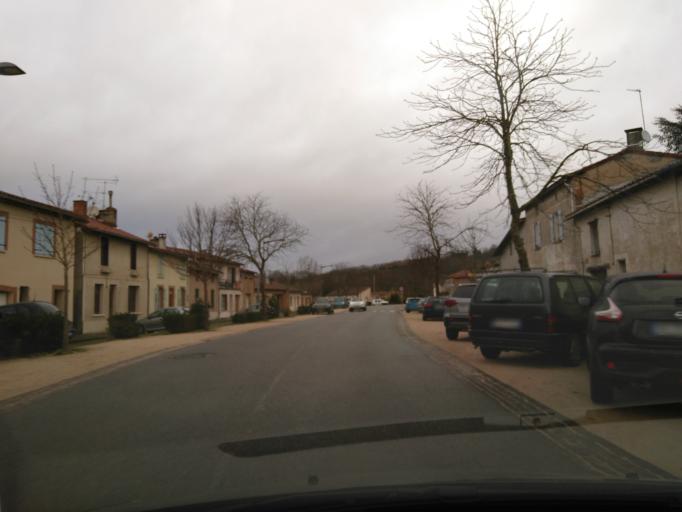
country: FR
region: Midi-Pyrenees
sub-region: Departement de la Haute-Garonne
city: Montesquieu-Volvestre
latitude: 43.2073
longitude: 1.2270
